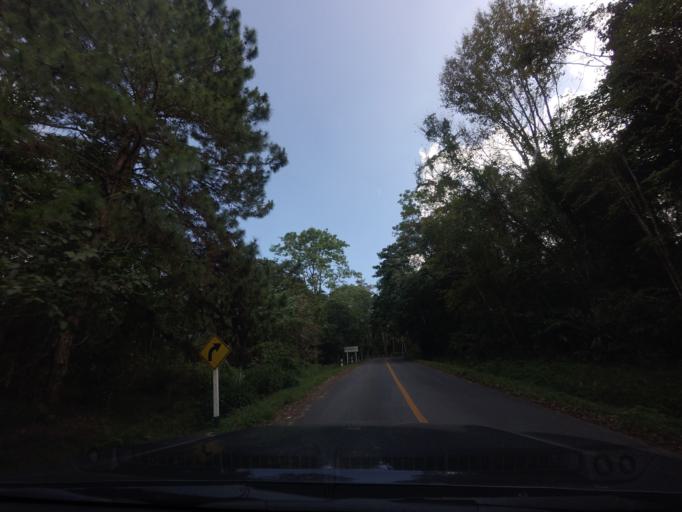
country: TH
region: Phitsanulok
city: Nakhon Thai
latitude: 16.9850
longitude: 101.0216
